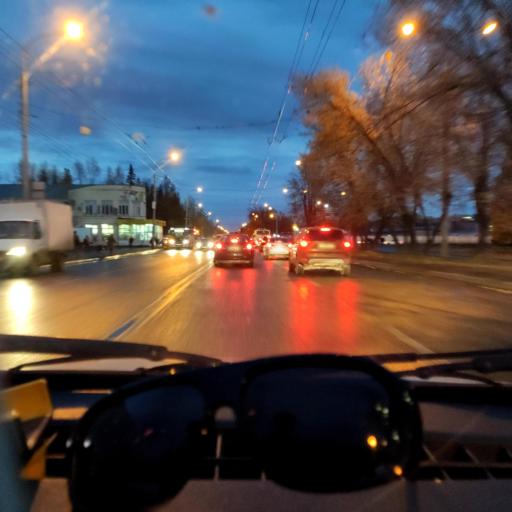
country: RU
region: Bashkortostan
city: Ufa
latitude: 54.7984
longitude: 56.1392
